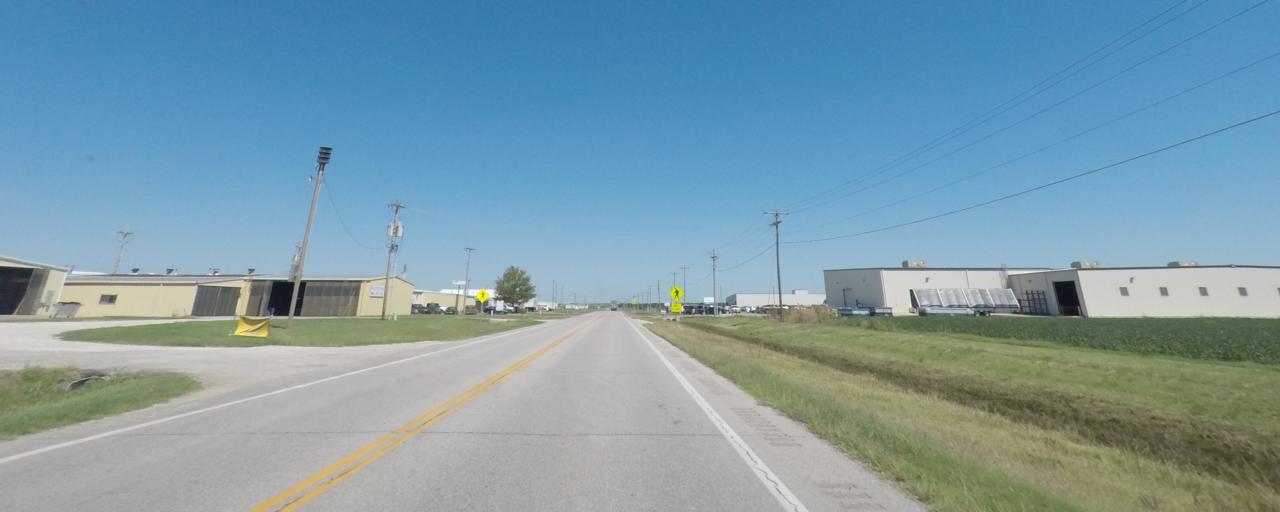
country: US
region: Kansas
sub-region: Sumner County
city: Wellington
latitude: 37.3213
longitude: -97.3848
